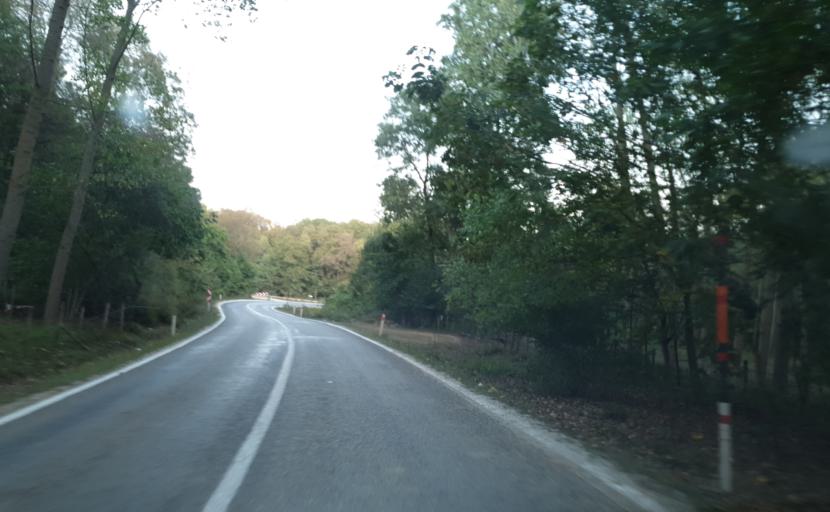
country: TR
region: Kirklareli
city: Igneada
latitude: 41.8751
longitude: 27.9164
